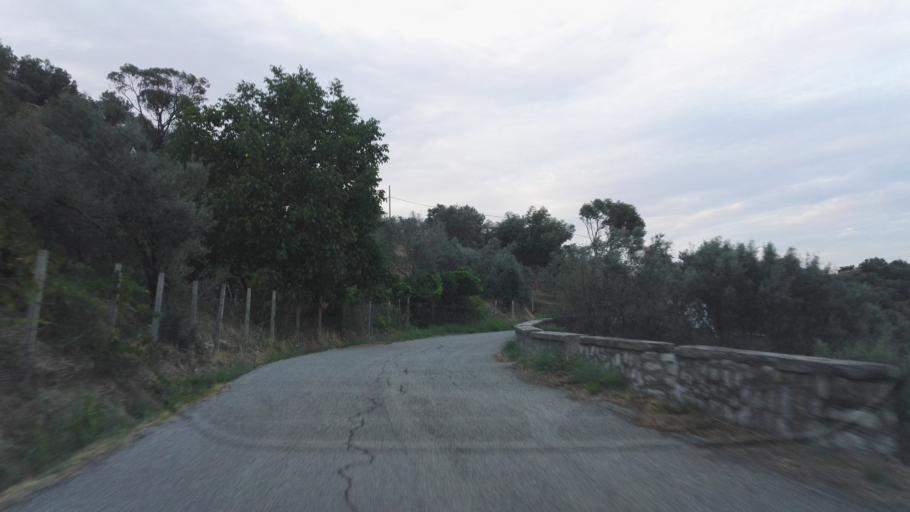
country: IT
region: Calabria
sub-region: Provincia di Reggio Calabria
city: Caulonia
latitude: 38.3879
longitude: 16.3994
